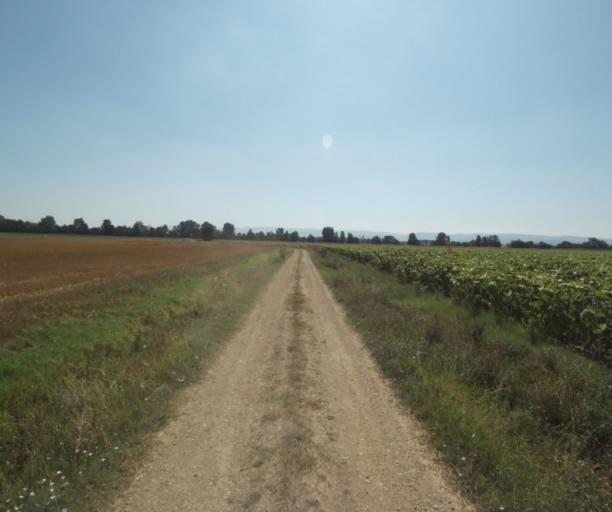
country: FR
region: Midi-Pyrenees
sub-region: Departement de la Haute-Garonne
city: Revel
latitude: 43.5164
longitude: 1.9617
